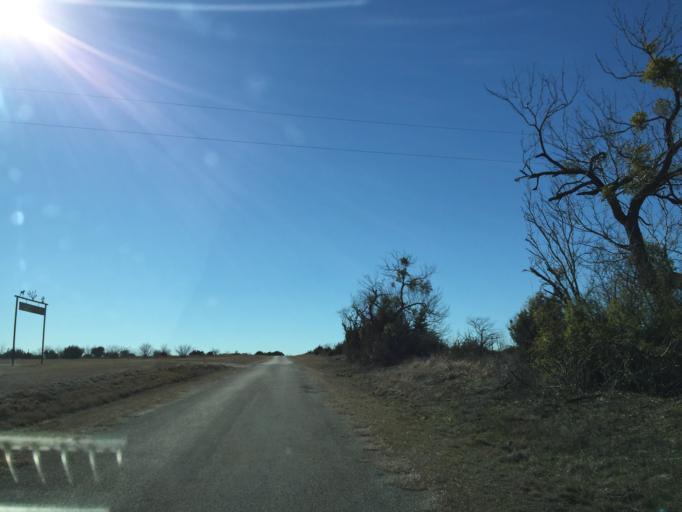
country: US
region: Texas
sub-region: Lampasas County
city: Lampasas
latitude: 30.9344
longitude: -98.1771
